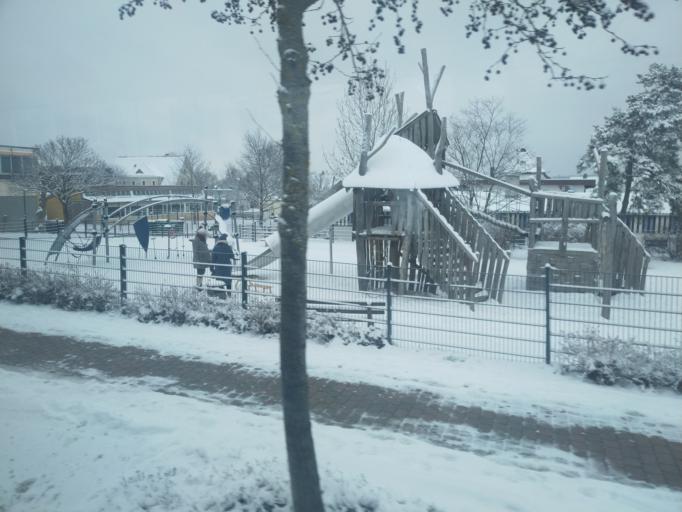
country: DE
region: Baden-Wuerttemberg
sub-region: Karlsruhe Region
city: Birkenfeld
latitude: 48.8723
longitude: 8.6376
